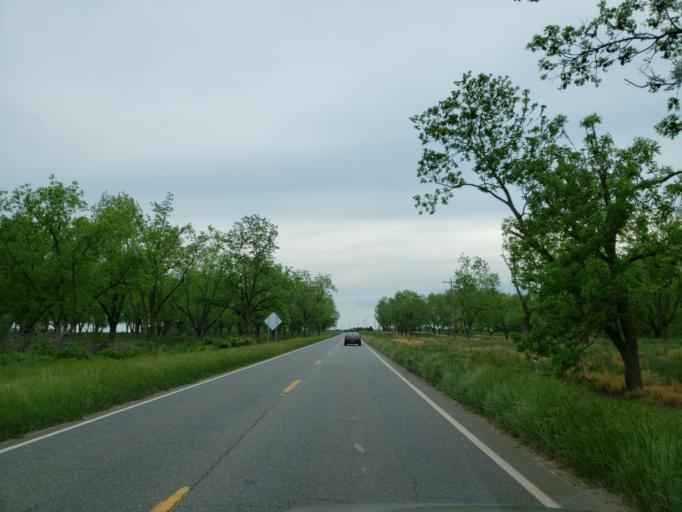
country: US
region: Georgia
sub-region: Macon County
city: Montezuma
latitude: 32.3532
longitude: -83.9696
